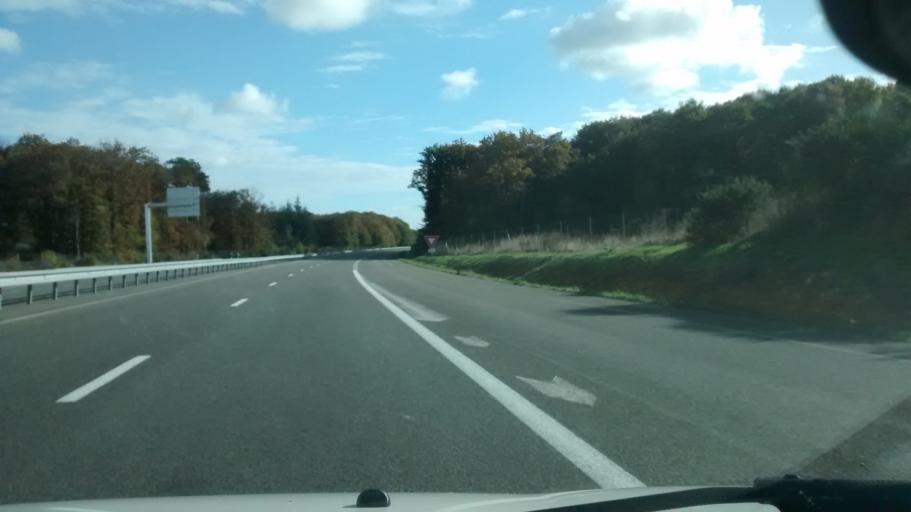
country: FR
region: Pays de la Loire
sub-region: Departement de Maine-et-Loire
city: Combree
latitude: 47.7307
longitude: -1.0719
